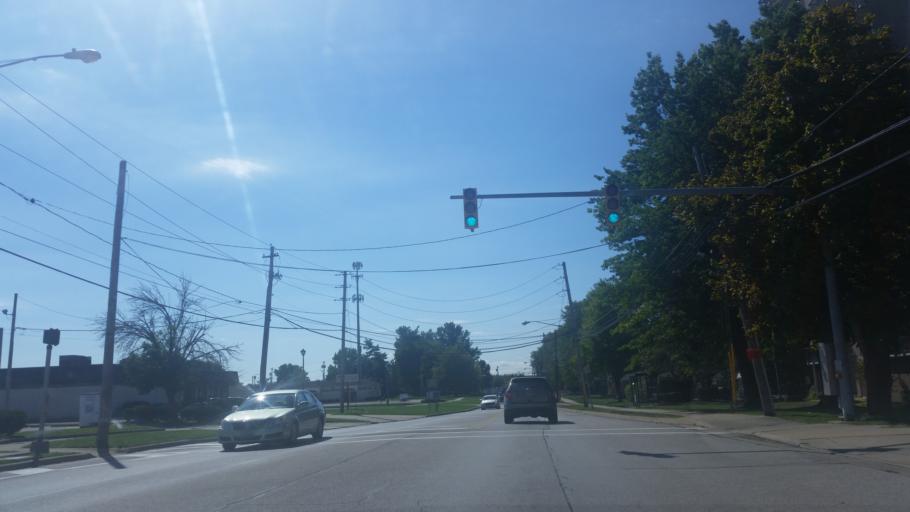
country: US
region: Ohio
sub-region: Summit County
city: Barberton
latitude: 41.0075
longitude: -81.5900
